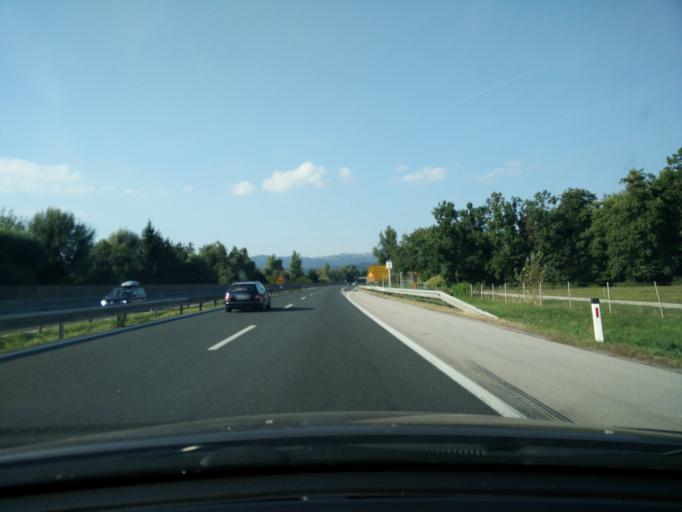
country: SI
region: Vrhnika
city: Verd
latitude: 45.9631
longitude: 14.3052
